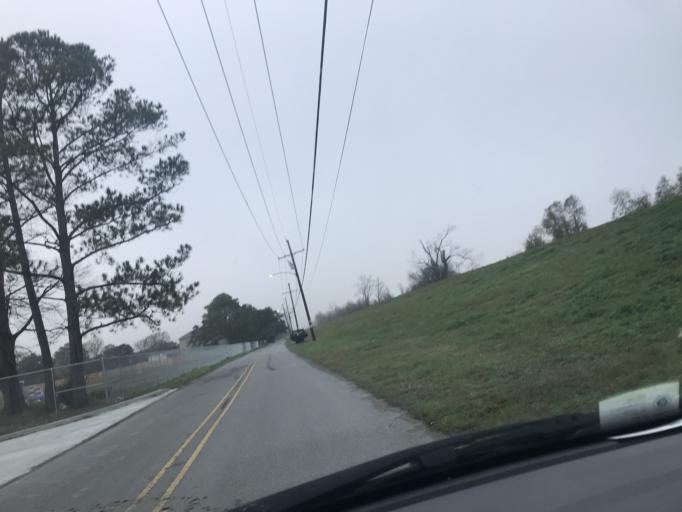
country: US
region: Louisiana
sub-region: Saint Bernard Parish
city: Arabi
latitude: 29.9376
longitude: -90.0060
